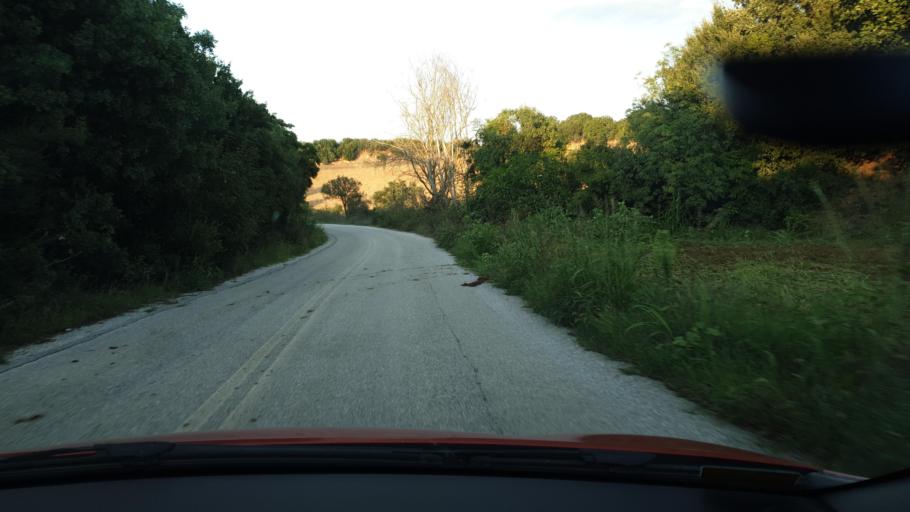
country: GR
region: Central Macedonia
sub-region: Nomos Thessalonikis
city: Nea Apollonia
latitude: 40.5501
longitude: 23.4502
